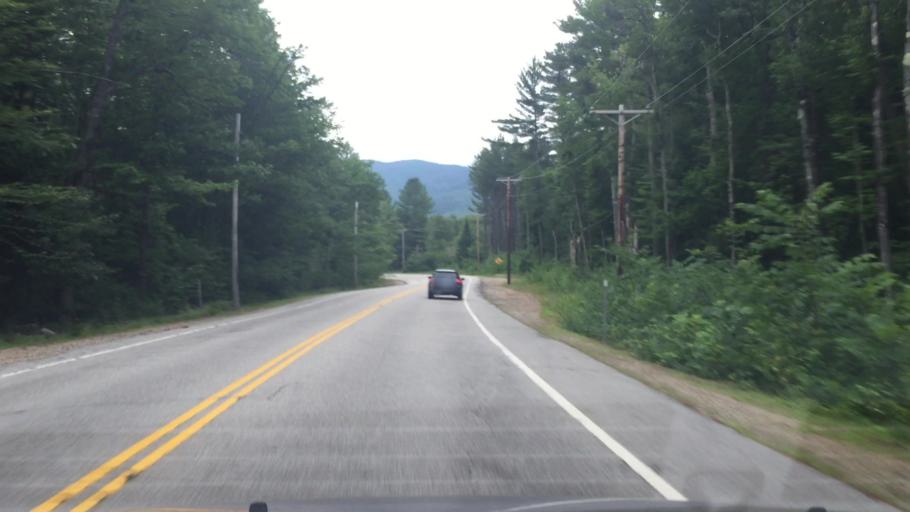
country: US
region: New Hampshire
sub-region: Carroll County
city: North Conway
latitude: 44.0745
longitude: -71.3054
